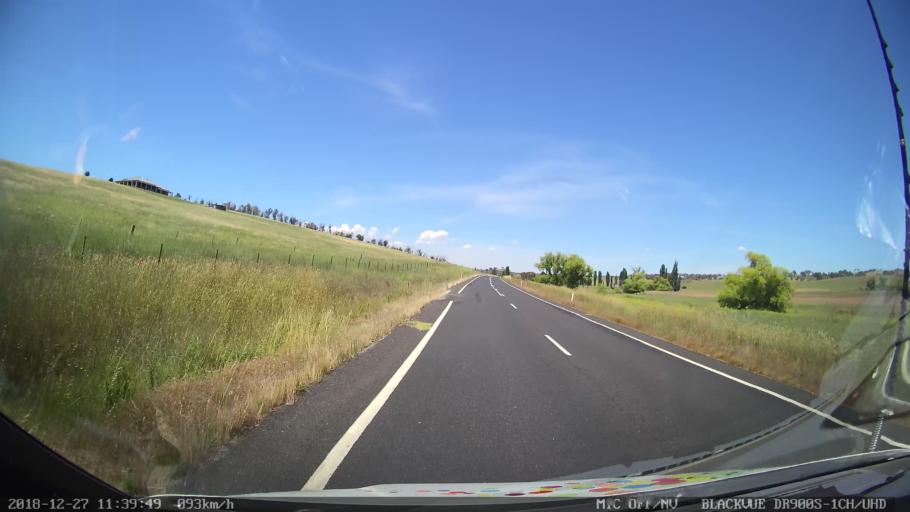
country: AU
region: New South Wales
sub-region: Bathurst Regional
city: Perthville
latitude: -33.5172
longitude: 149.4953
